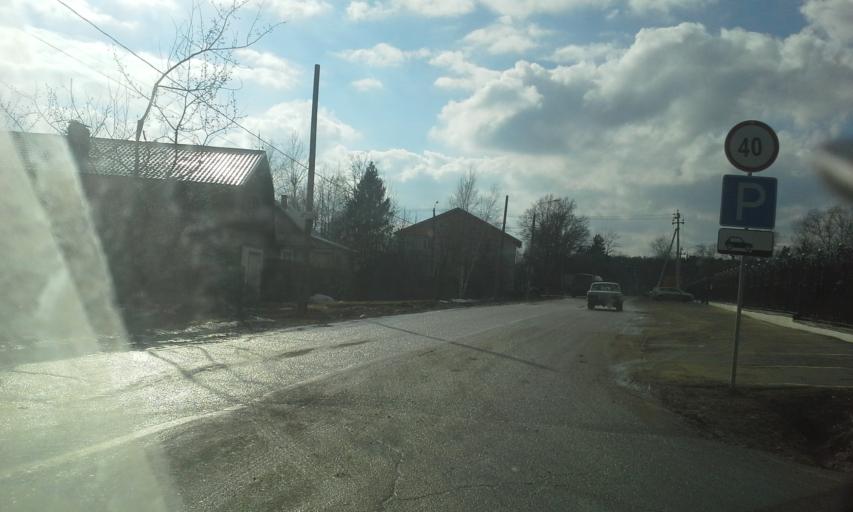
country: RU
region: Moscow
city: Tolstopal'tsevo
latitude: 55.6111
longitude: 37.2081
